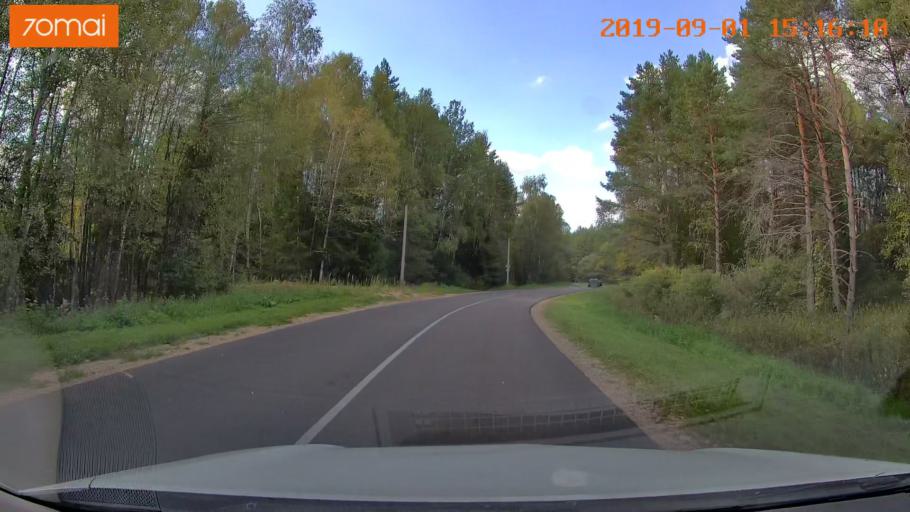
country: RU
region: Kaluga
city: Maloyaroslavets
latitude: 54.8846
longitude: 36.5299
